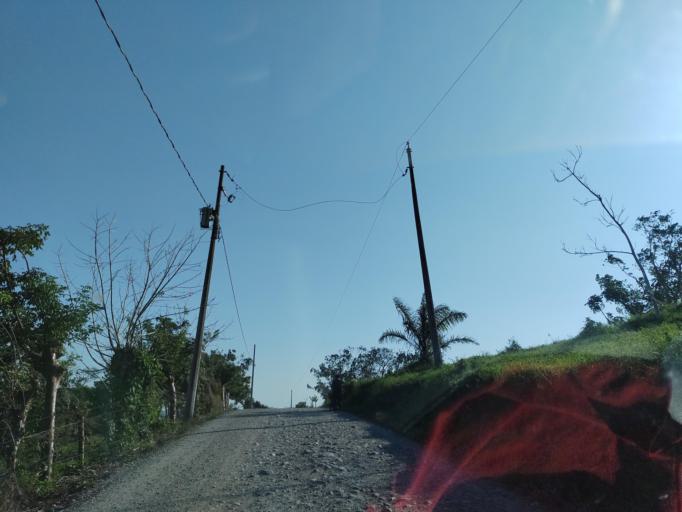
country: MX
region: Veracruz
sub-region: Papantla
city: Polutla
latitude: 20.4557
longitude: -97.2411
